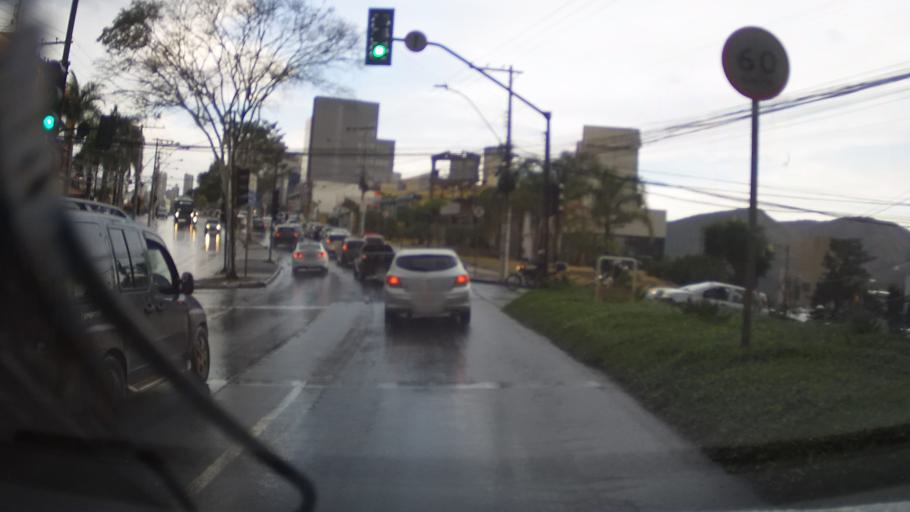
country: BR
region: Minas Gerais
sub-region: Belo Horizonte
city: Belo Horizonte
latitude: -19.9617
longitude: -43.9573
